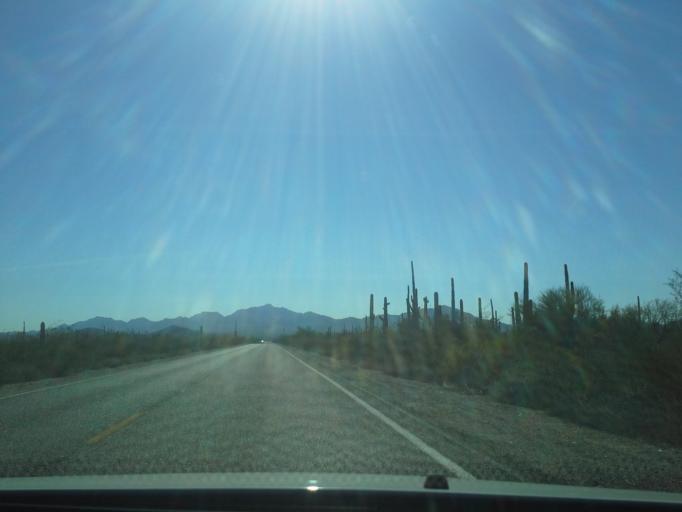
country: MX
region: Sonora
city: Sonoyta
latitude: 31.9003
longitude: -112.8115
